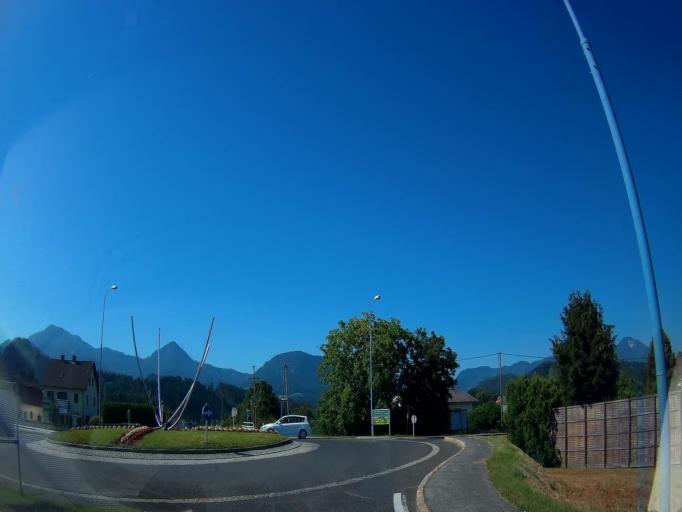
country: AT
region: Carinthia
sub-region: Politischer Bezirk Volkermarkt
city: Eberndorf
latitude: 46.5762
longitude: 14.6278
